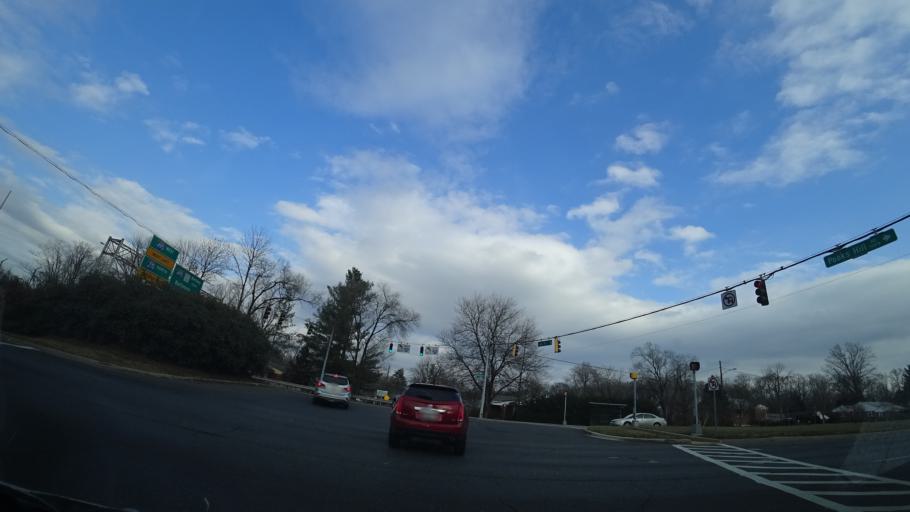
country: US
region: Maryland
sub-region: Montgomery County
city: South Kensington
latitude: 39.0149
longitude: -77.1000
